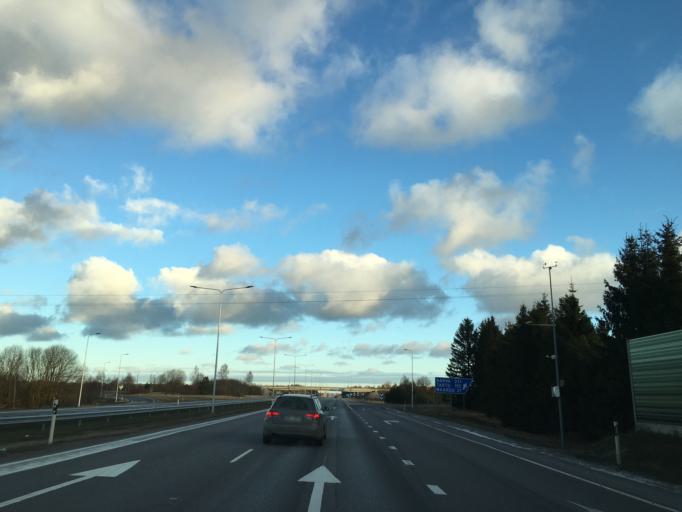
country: EE
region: Harju
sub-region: Saue linn
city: Saue
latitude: 59.3098
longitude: 24.5705
